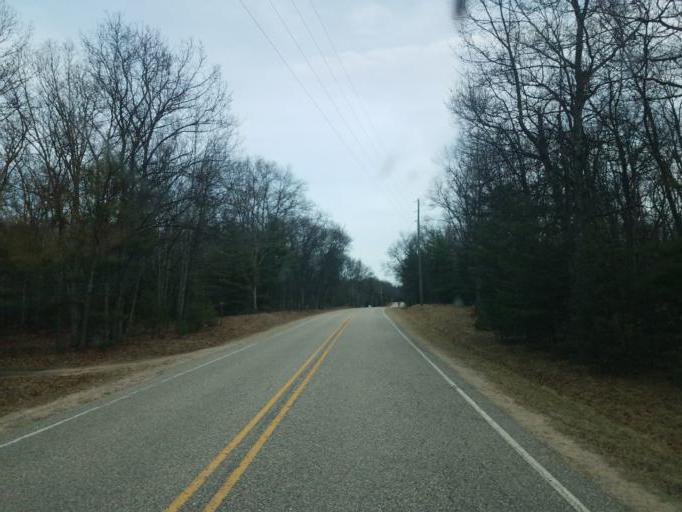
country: US
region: Michigan
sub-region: Oceana County
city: Hart
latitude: 43.7568
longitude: -86.4470
